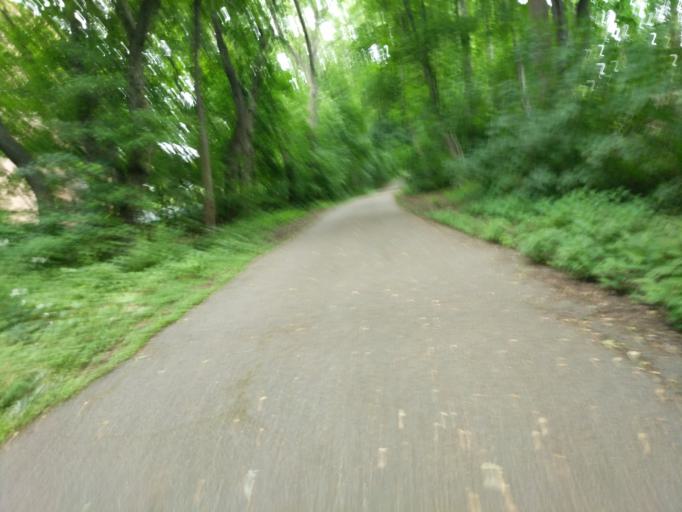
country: US
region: New York
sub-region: Nassau County
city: Bellerose Terrace
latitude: 40.7355
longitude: -73.7619
